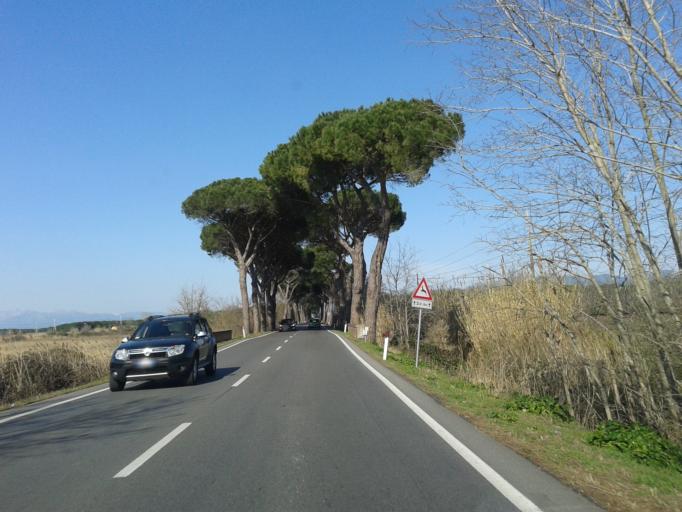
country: IT
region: Tuscany
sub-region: Provincia di Livorno
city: Guasticce
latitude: 43.6484
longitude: 10.3618
